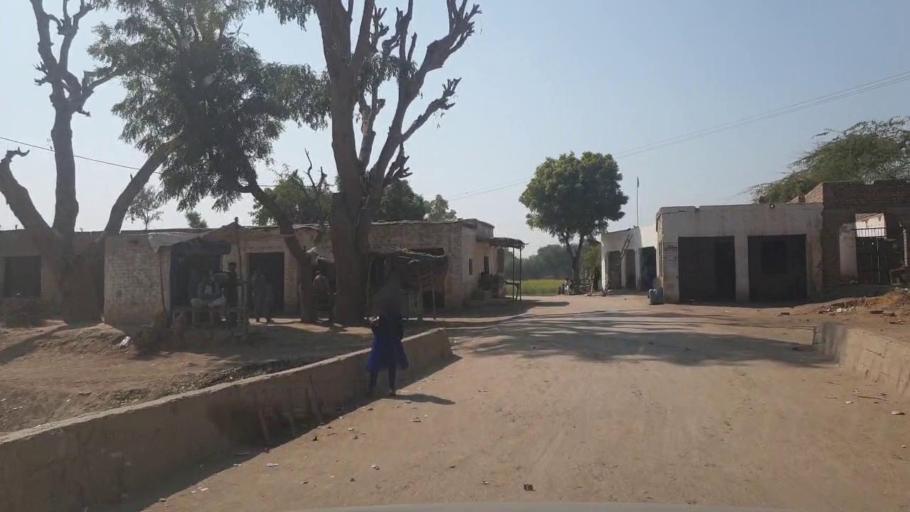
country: PK
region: Sindh
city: Chambar
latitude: 25.2549
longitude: 68.8338
